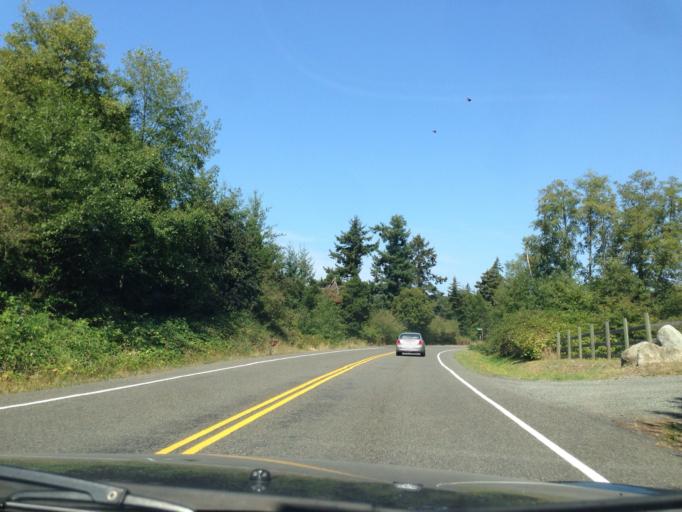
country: US
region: Washington
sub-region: San Juan County
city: Friday Harbor
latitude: 48.5028
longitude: -123.0357
